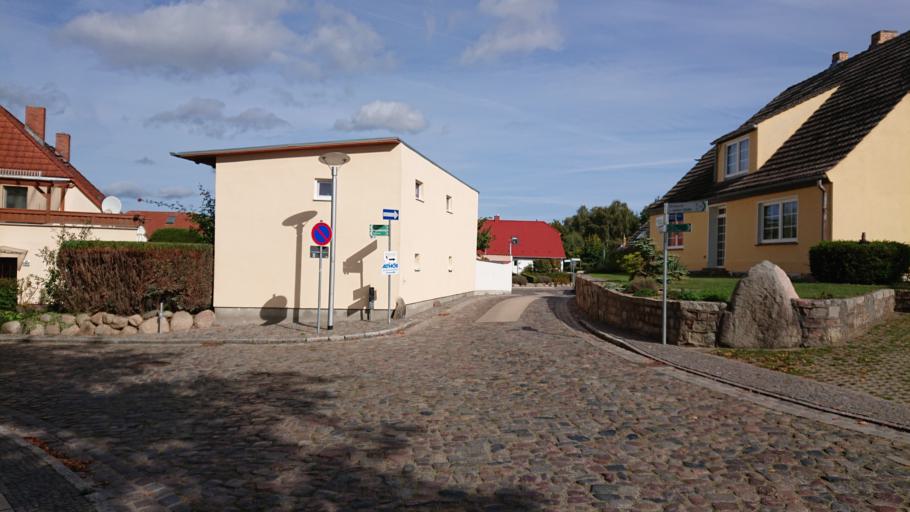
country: DE
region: Mecklenburg-Vorpommern
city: Altefahr
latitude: 54.3302
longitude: 13.1261
